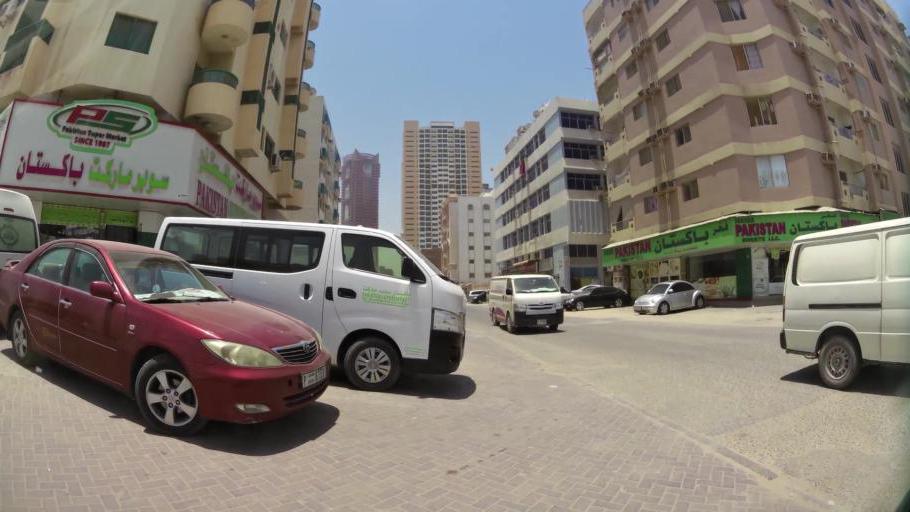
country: AE
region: Ajman
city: Ajman
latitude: 25.3973
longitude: 55.4343
